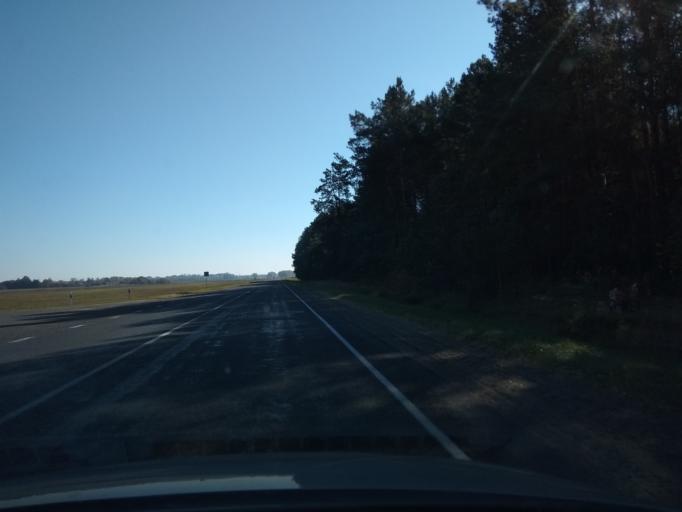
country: BY
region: Brest
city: Malaryta
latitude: 51.9450
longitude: 24.0232
